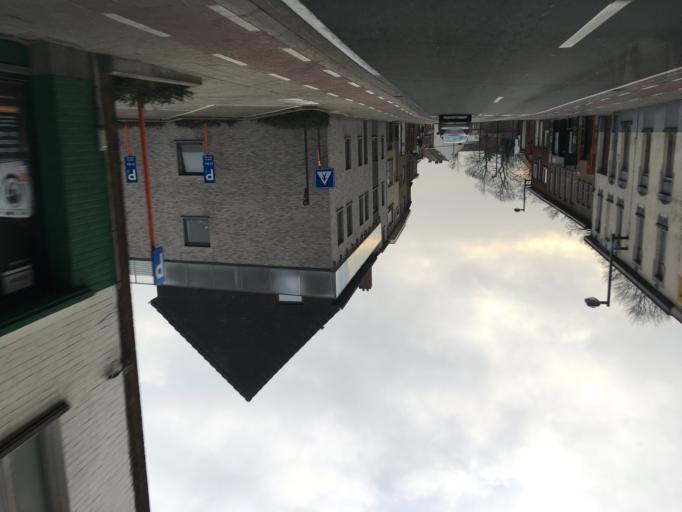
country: BE
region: Flanders
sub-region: Provincie West-Vlaanderen
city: Anzegem
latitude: 50.8357
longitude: 3.4767
